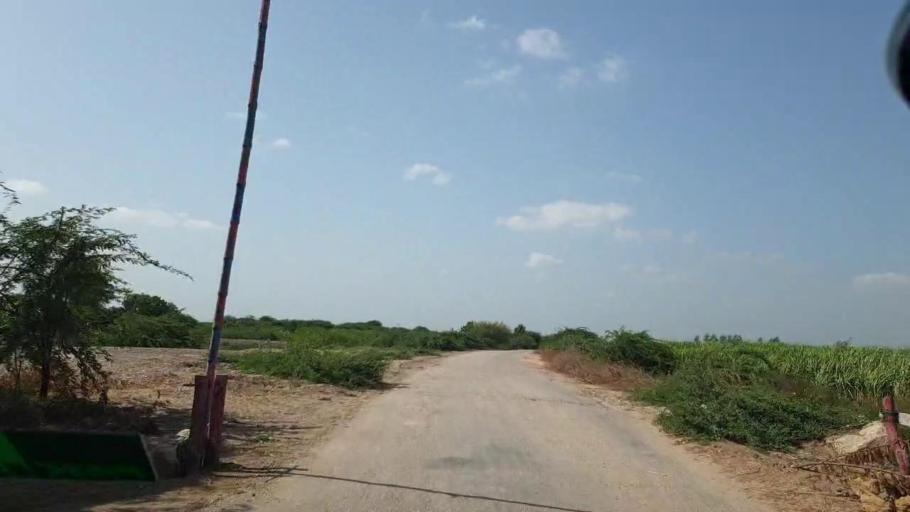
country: PK
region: Sindh
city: Tando Bago
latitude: 24.6761
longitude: 69.1922
